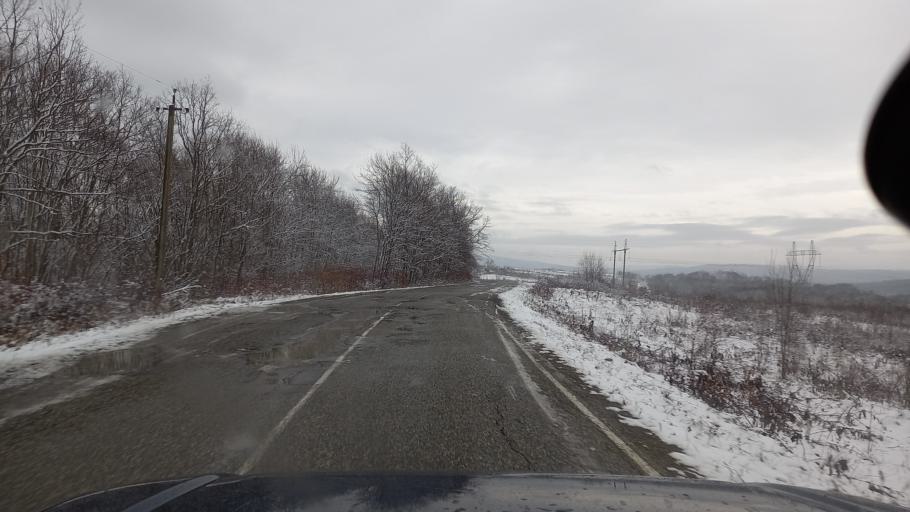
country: RU
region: Adygeya
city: Abadzekhskaya
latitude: 44.3487
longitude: 40.3618
